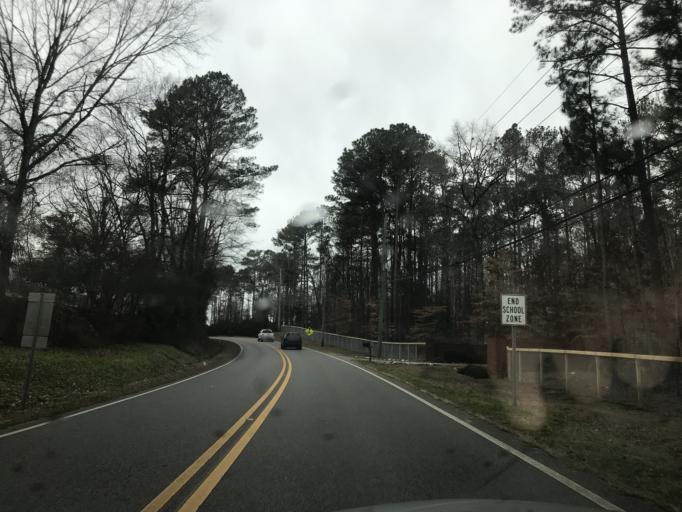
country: US
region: Alabama
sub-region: Shelby County
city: Meadowbrook
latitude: 33.3776
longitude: -86.7091
